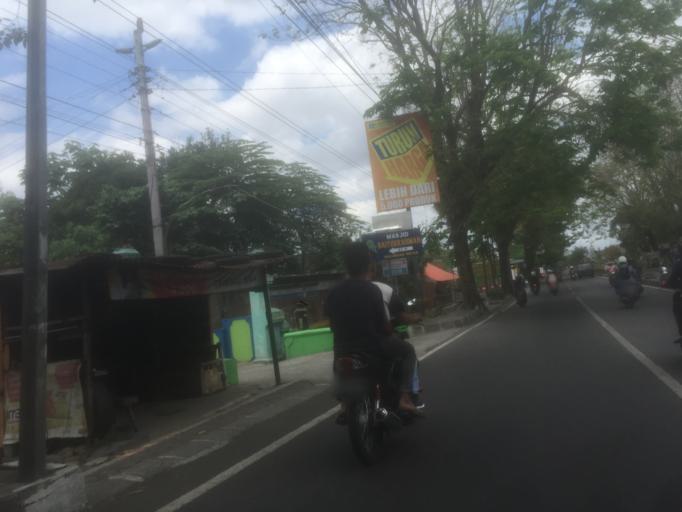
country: ID
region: Daerah Istimewa Yogyakarta
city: Melati
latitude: -7.7297
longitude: 110.3635
